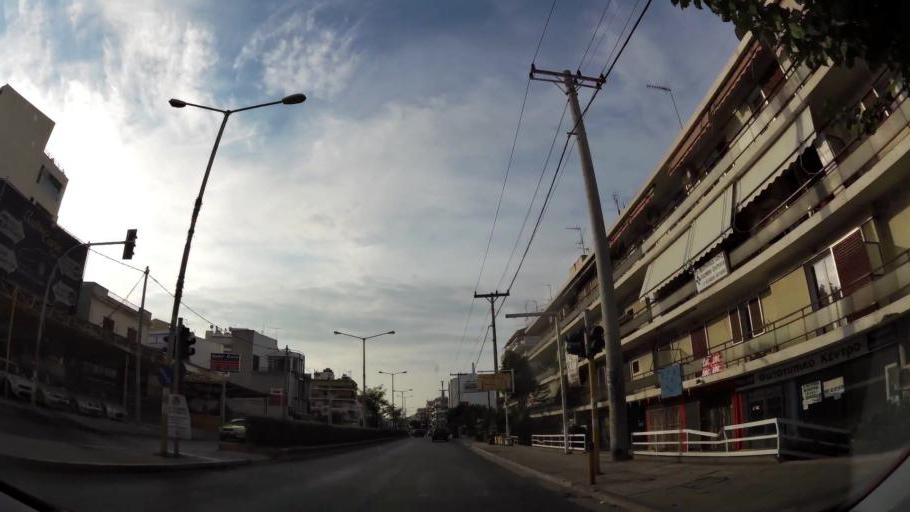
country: GR
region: Attica
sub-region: Nomarchia Athinas
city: Kallithea
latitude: 37.9392
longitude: 23.7008
